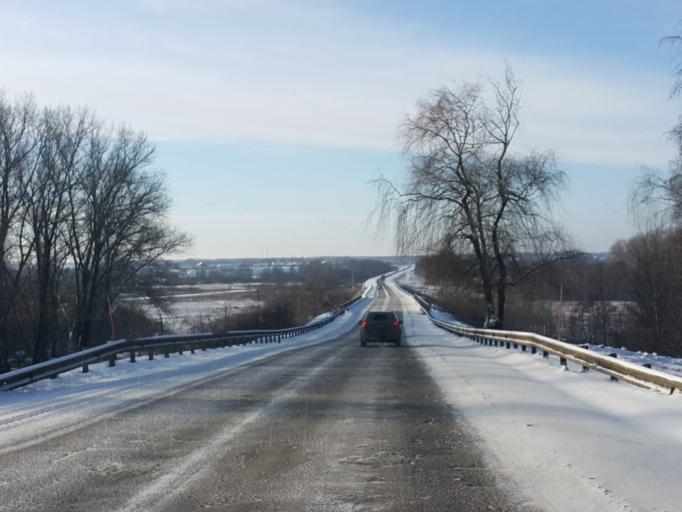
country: RU
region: Tambov
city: Znamenka
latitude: 52.4166
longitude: 41.4861
